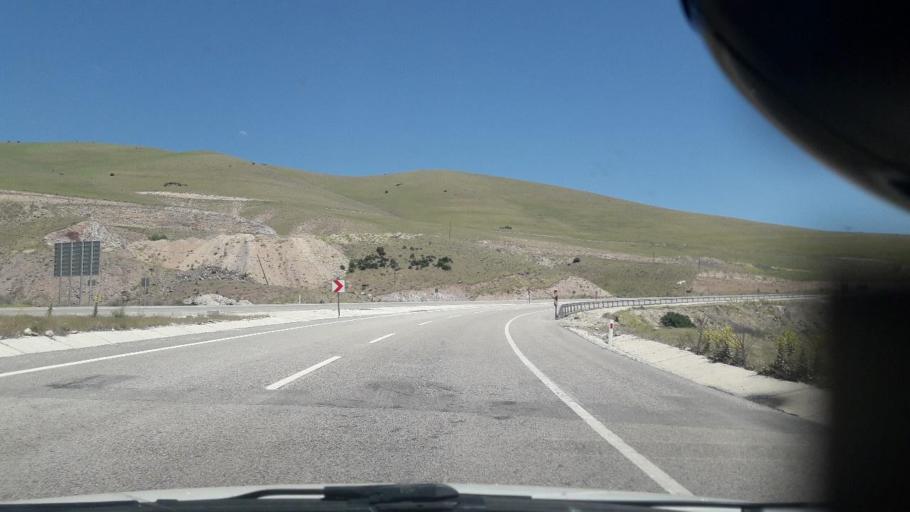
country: TR
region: Malatya
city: Yazihan
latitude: 38.6719
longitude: 38.1477
